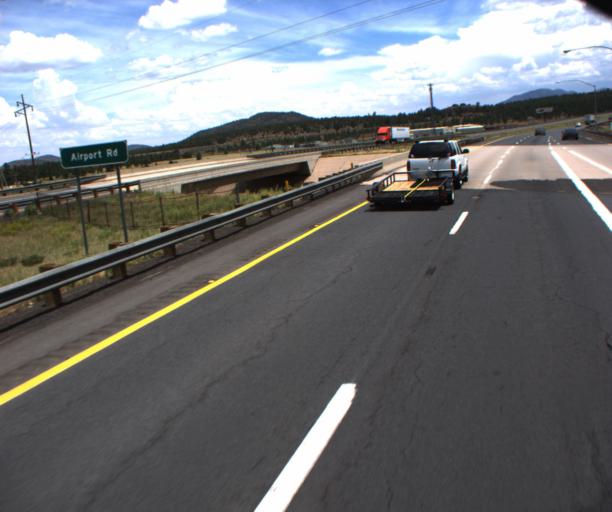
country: US
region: Arizona
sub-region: Coconino County
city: Williams
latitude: 35.2619
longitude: -112.1867
